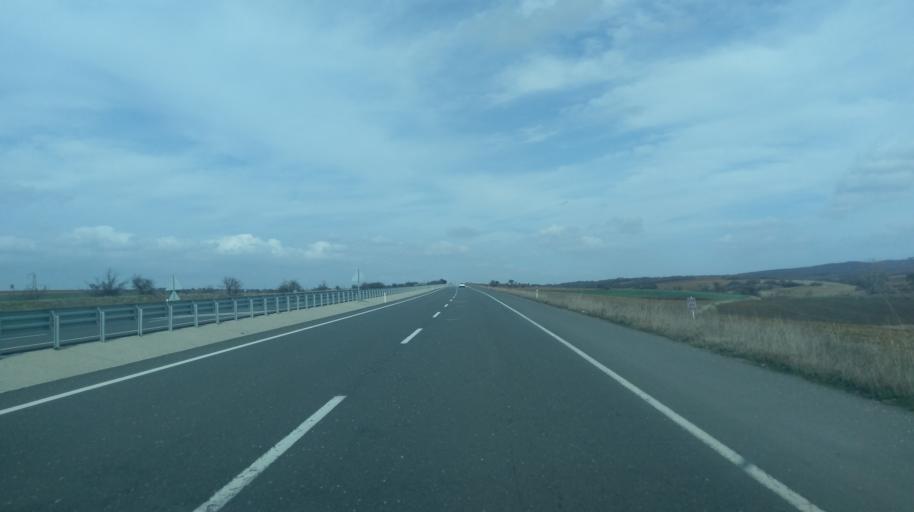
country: TR
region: Edirne
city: Hamidiye
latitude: 41.1161
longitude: 26.6511
